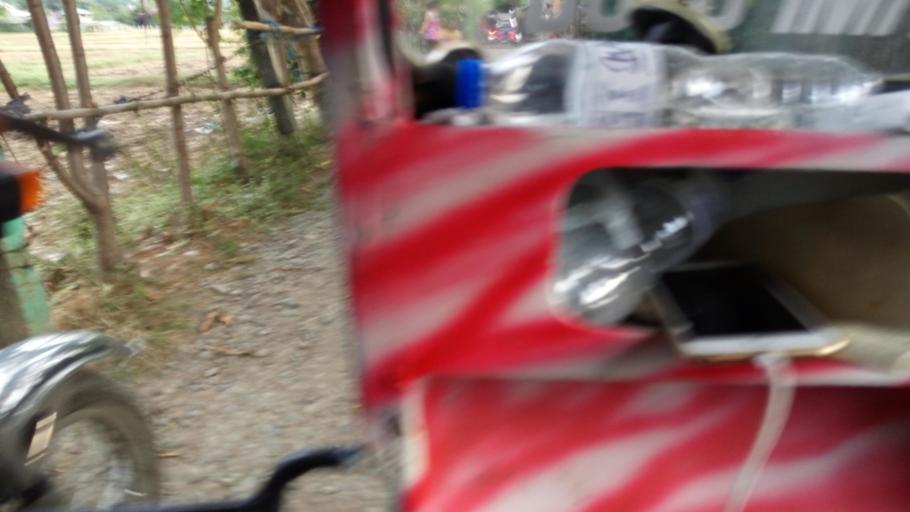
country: PH
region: Ilocos
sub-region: Province of La Union
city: Damortis
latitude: 16.2542
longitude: 120.4003
